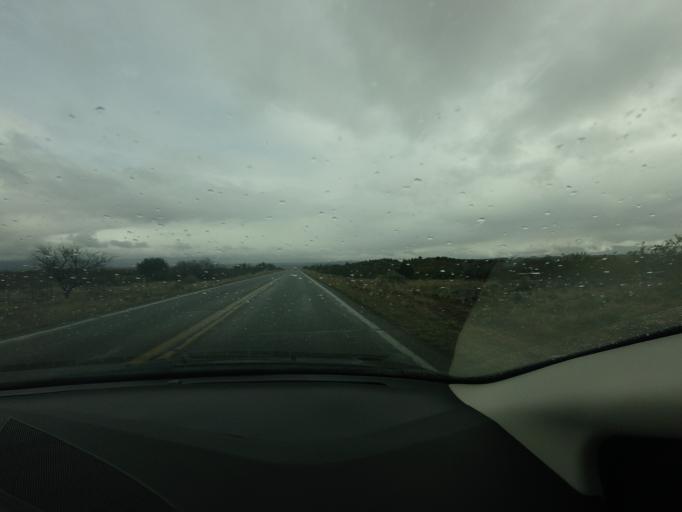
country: US
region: Arizona
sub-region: Yavapai County
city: Cornville
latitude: 34.6881
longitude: -111.8510
